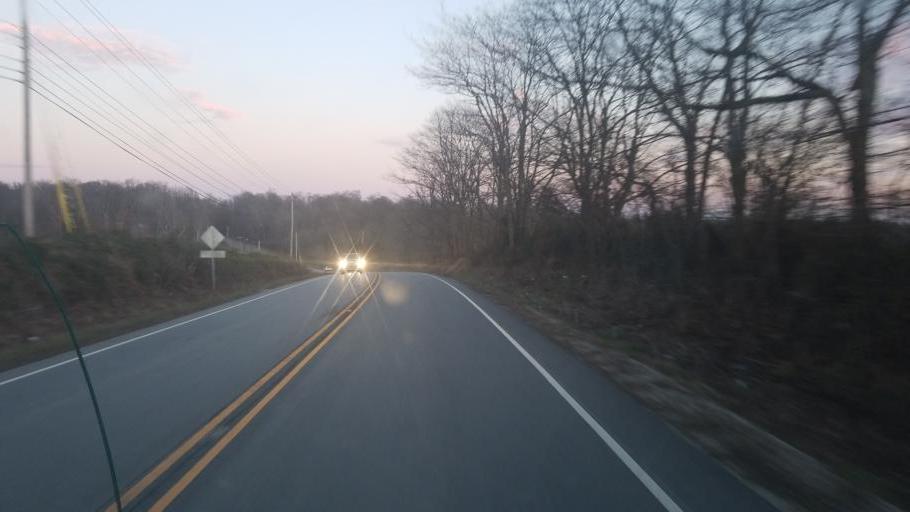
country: US
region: Indiana
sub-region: Lawrence County
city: Bedford
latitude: 38.8743
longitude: -86.3210
